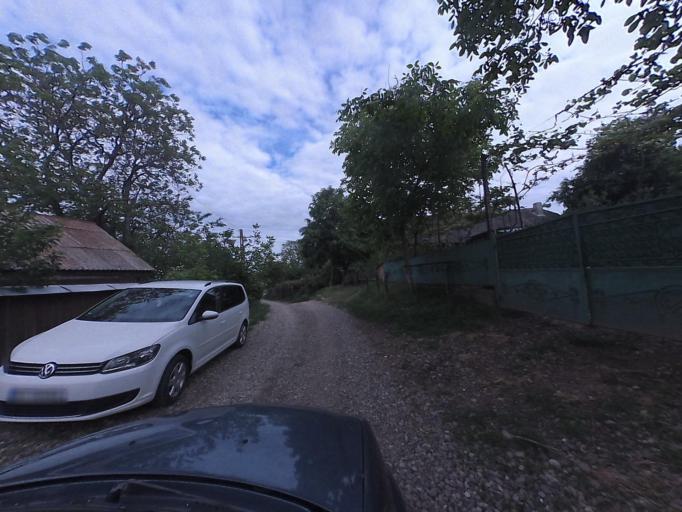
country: RO
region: Neamt
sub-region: Comuna Dulcesti
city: Dulcesti
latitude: 46.9557
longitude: 26.7929
